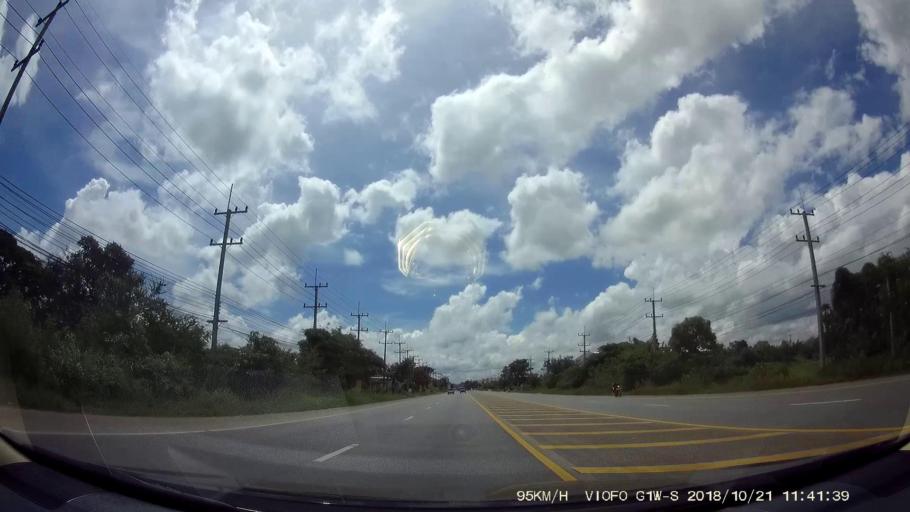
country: TH
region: Chaiyaphum
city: Chaiyaphum
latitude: 15.6960
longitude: 102.0137
